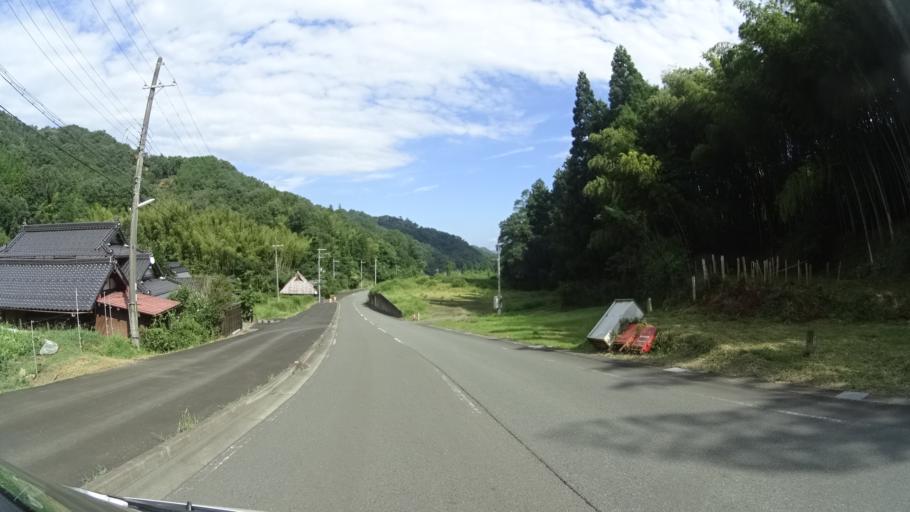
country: JP
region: Kyoto
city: Fukuchiyama
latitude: 35.3421
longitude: 135.1623
